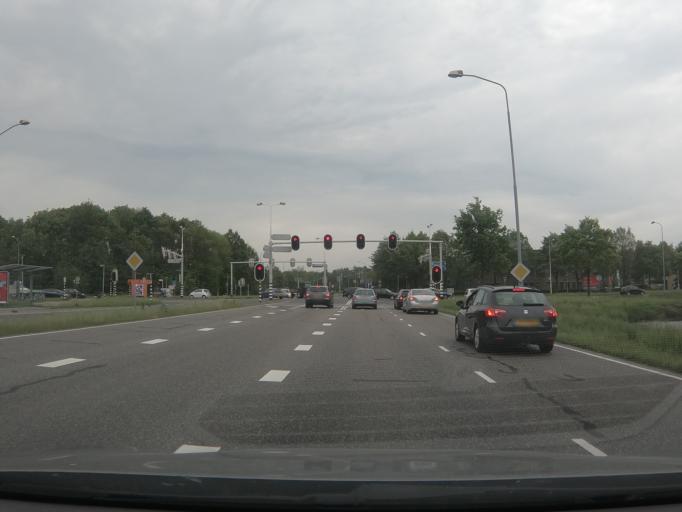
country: NL
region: Drenthe
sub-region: Gemeente Assen
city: Assen
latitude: 52.9947
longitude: 6.5311
